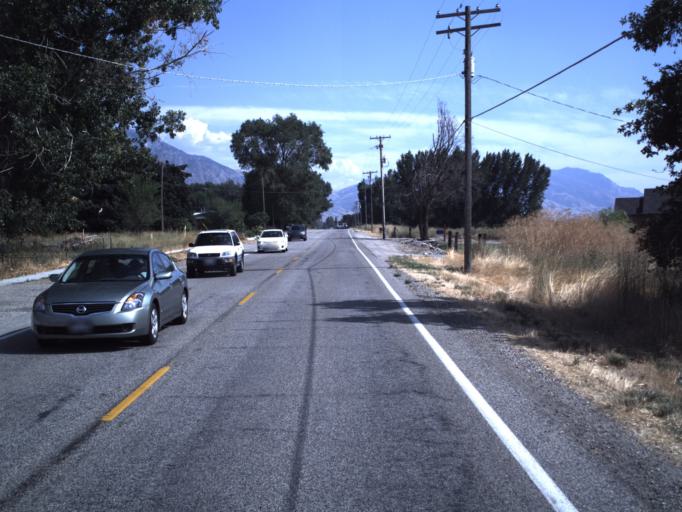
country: US
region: Utah
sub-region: Box Elder County
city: Honeyville
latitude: 41.6218
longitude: -112.0713
